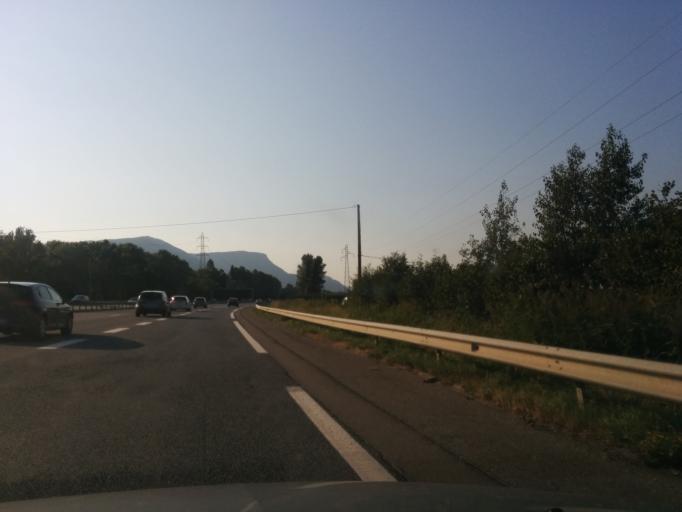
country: FR
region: Rhone-Alpes
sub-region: Departement de l'Isere
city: Saint-Egreve
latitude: 45.2187
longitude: 5.6753
